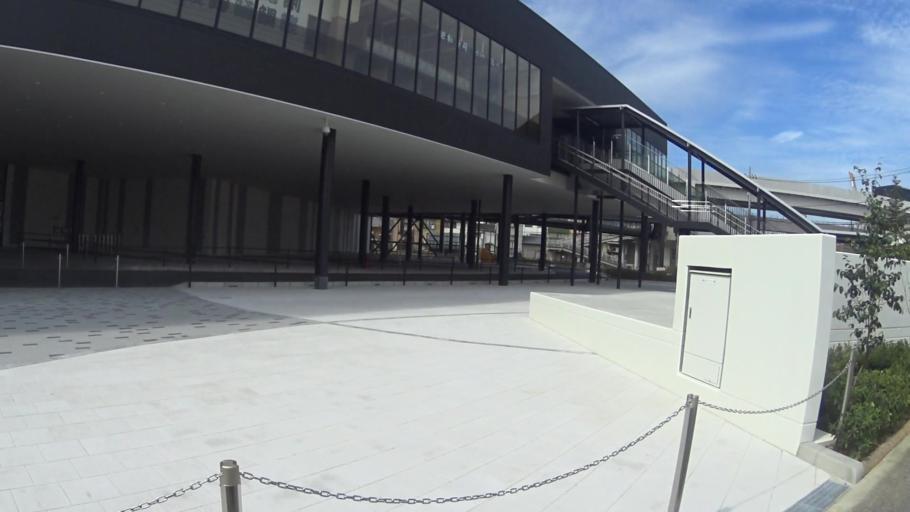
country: JP
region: Kyoto
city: Muko
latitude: 34.9644
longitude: 135.7072
